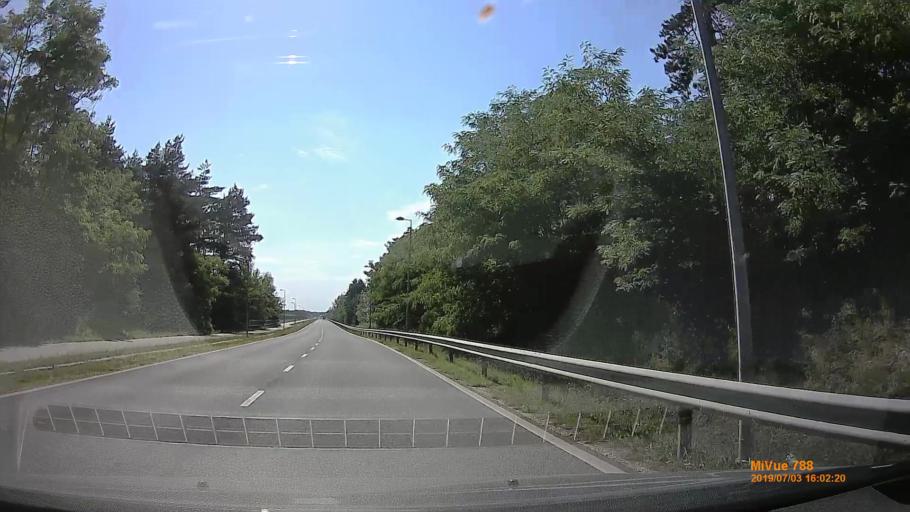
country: HU
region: Gyor-Moson-Sopron
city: Gyor
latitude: 47.7067
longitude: 17.7092
